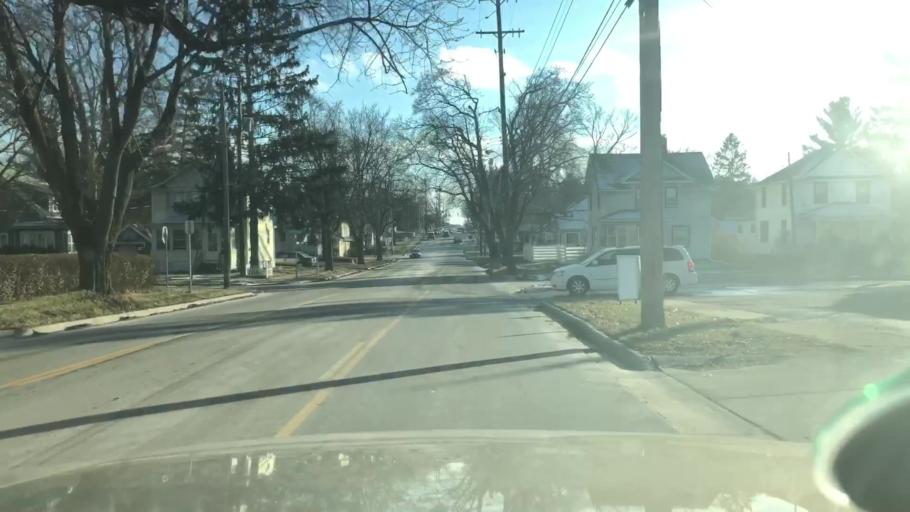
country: US
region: Michigan
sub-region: Jackson County
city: Jackson
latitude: 42.2324
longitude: -84.4233
